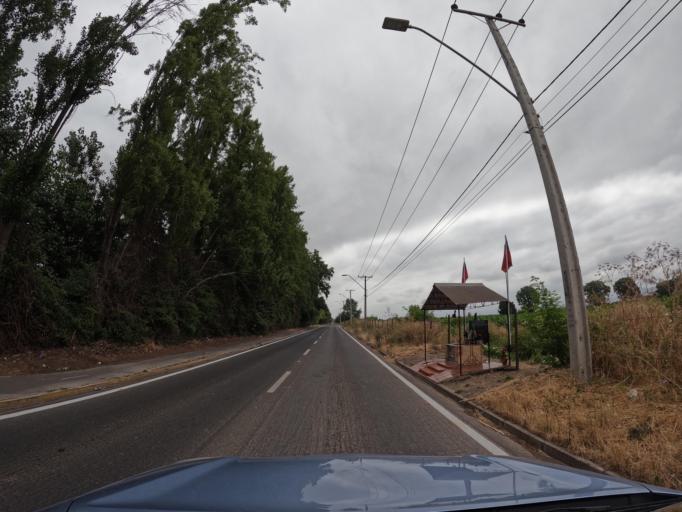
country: CL
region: O'Higgins
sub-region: Provincia de Colchagua
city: Chimbarongo
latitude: -34.7319
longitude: -71.0611
